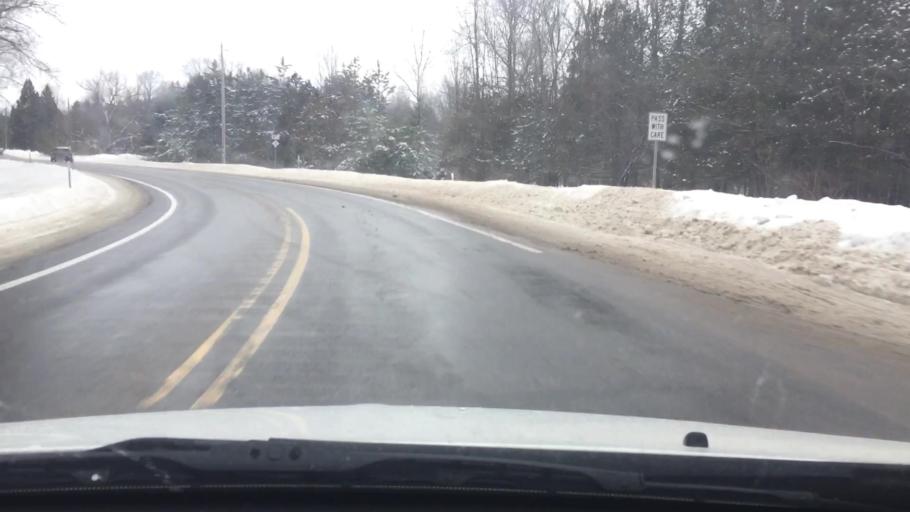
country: US
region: Michigan
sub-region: Charlevoix County
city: East Jordan
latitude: 45.1324
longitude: -85.0822
